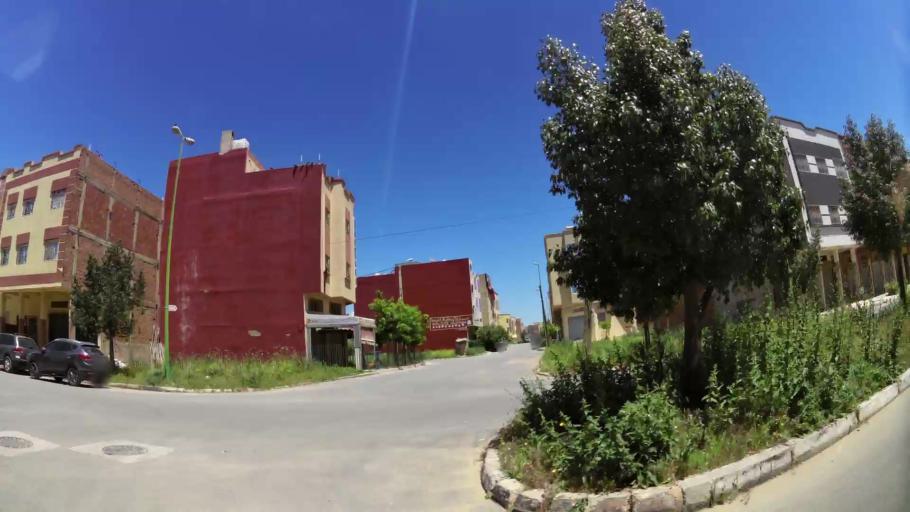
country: MA
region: Meknes-Tafilalet
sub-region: Meknes
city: Meknes
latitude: 33.8496
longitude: -5.5528
